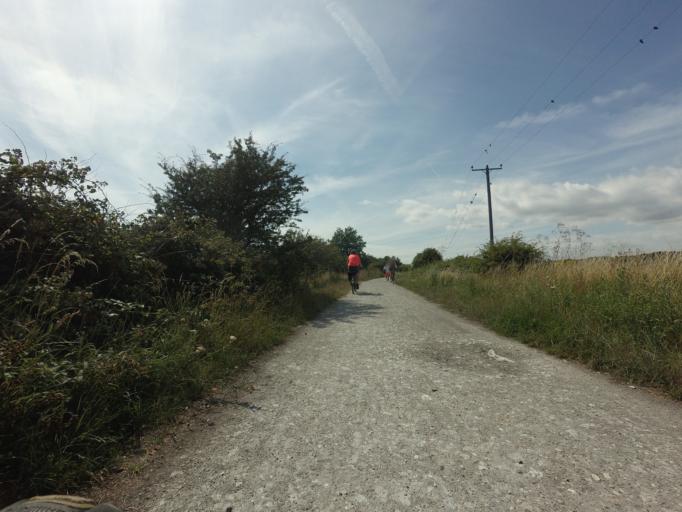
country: GB
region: England
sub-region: East Sussex
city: Rye
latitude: 50.9489
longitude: 0.7510
